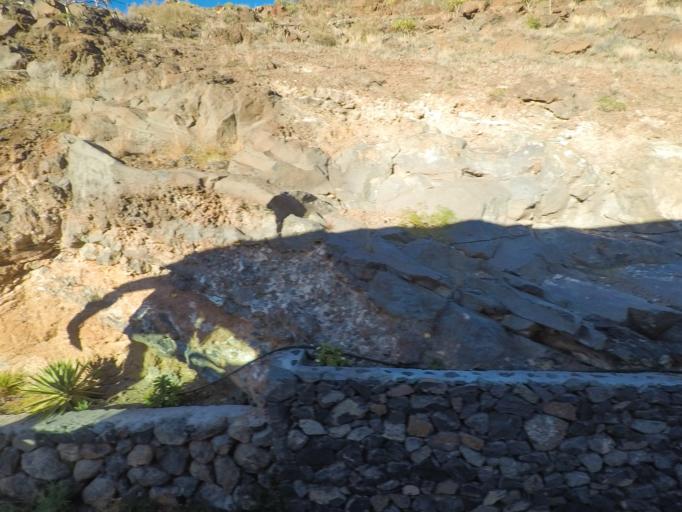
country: ES
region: Canary Islands
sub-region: Provincia de Santa Cruz de Tenerife
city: San Sebastian de la Gomera
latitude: 28.0899
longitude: -17.1180
